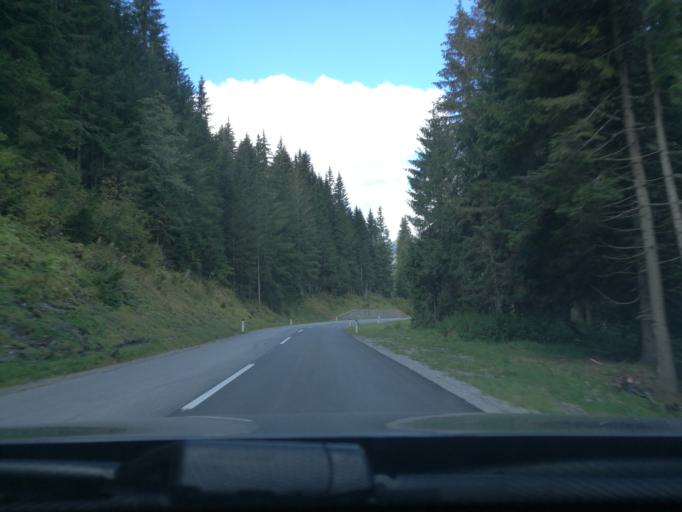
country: AT
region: Tyrol
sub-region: Politischer Bezirk Schwaz
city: Gerlos
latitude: 47.2369
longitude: 12.0766
